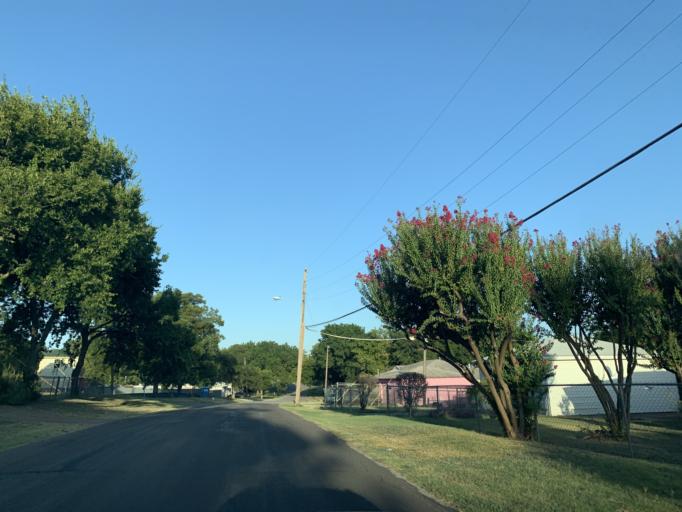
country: US
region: Texas
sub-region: Dallas County
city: Dallas
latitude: 32.6986
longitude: -96.8094
